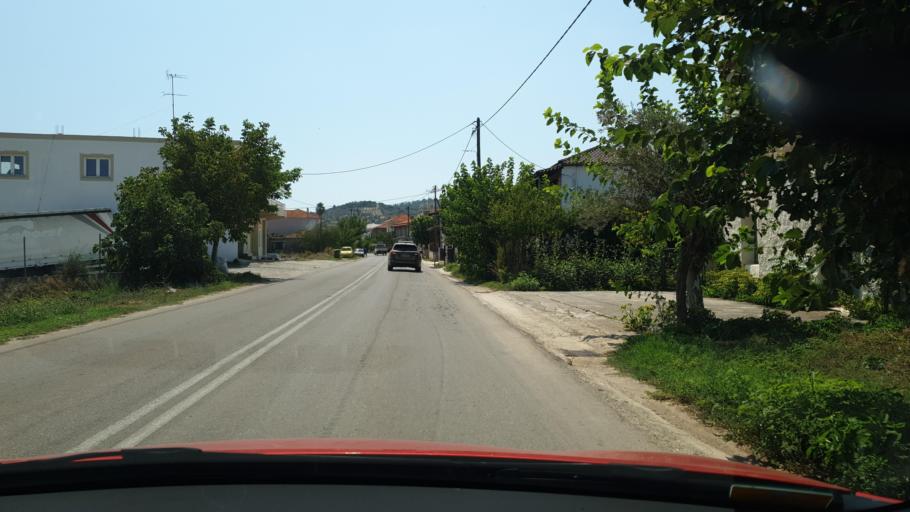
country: GR
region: Central Greece
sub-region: Nomos Evvoias
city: Aliveri
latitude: 38.4524
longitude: 24.1136
